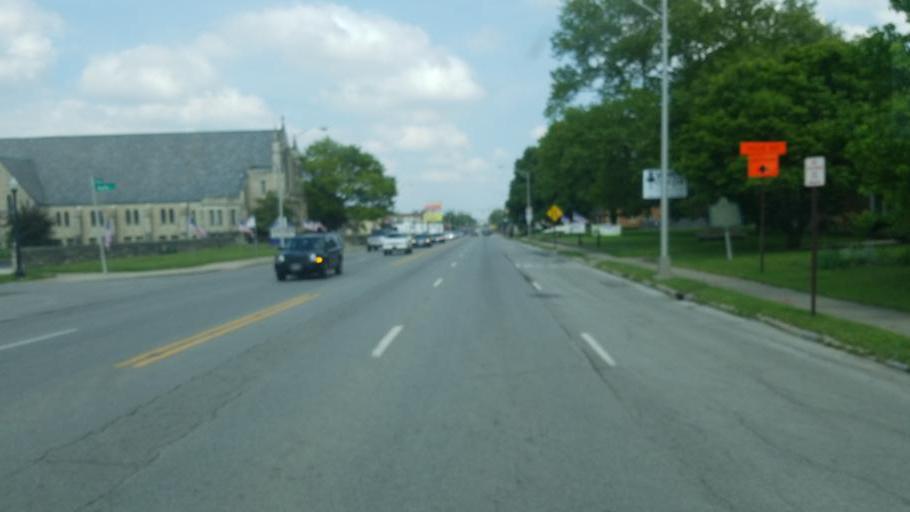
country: US
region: Ohio
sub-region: Franklin County
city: Upper Arlington
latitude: 39.9546
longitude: -83.0797
